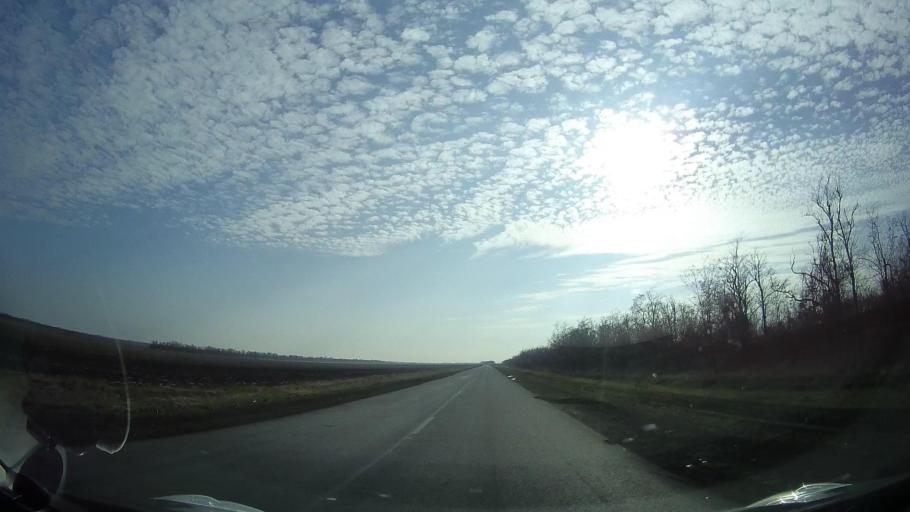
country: RU
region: Rostov
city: Veselyy
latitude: 46.9750
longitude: 40.7198
